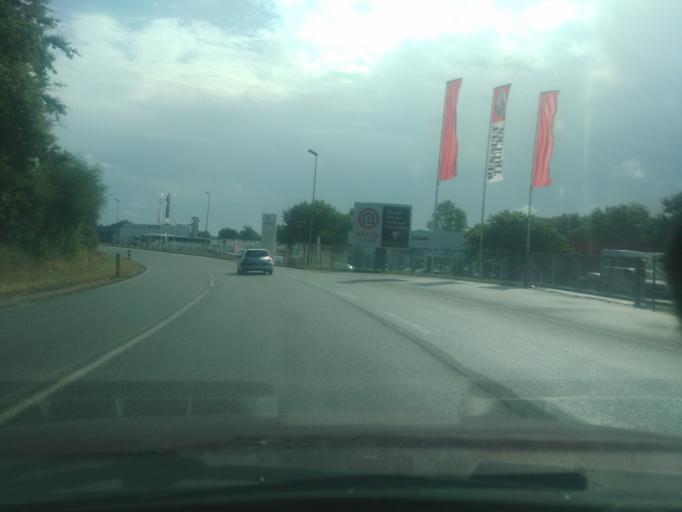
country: FR
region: Poitou-Charentes
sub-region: Departement des Deux-Sevres
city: Chatillon-sur-Thouet
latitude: 46.6442
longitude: -0.2211
